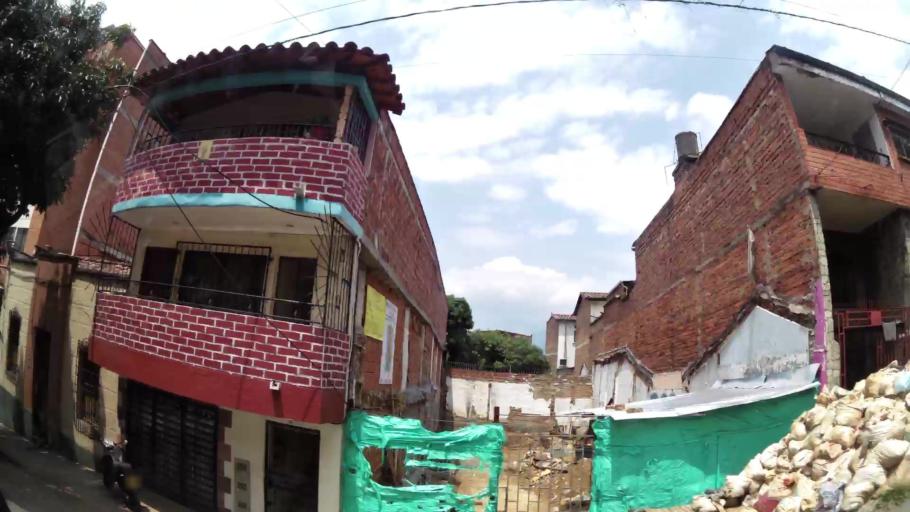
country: CO
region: Antioquia
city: Medellin
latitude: 6.2540
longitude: -75.5589
